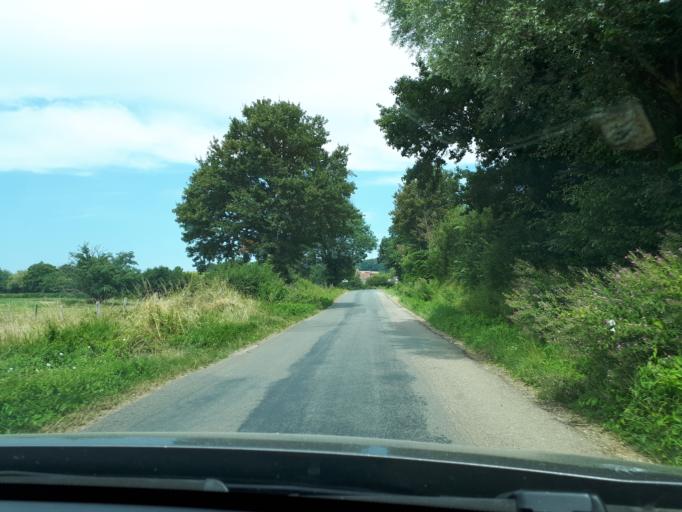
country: FR
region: Centre
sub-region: Departement du Cher
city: Sancerre
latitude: 47.3022
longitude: 2.7463
